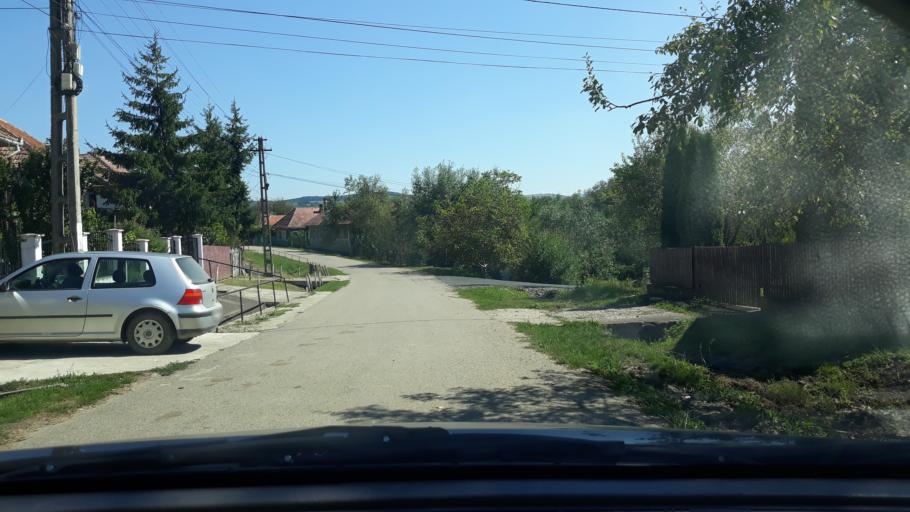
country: RO
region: Salaj
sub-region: Comuna Dobrin
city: Dobrin
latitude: 47.2973
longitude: 23.0894
